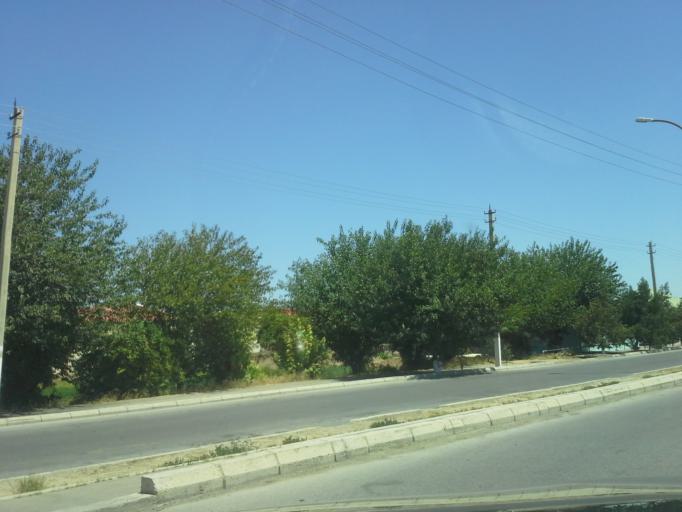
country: TM
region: Ahal
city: Abadan
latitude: 38.0287
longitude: 58.2633
